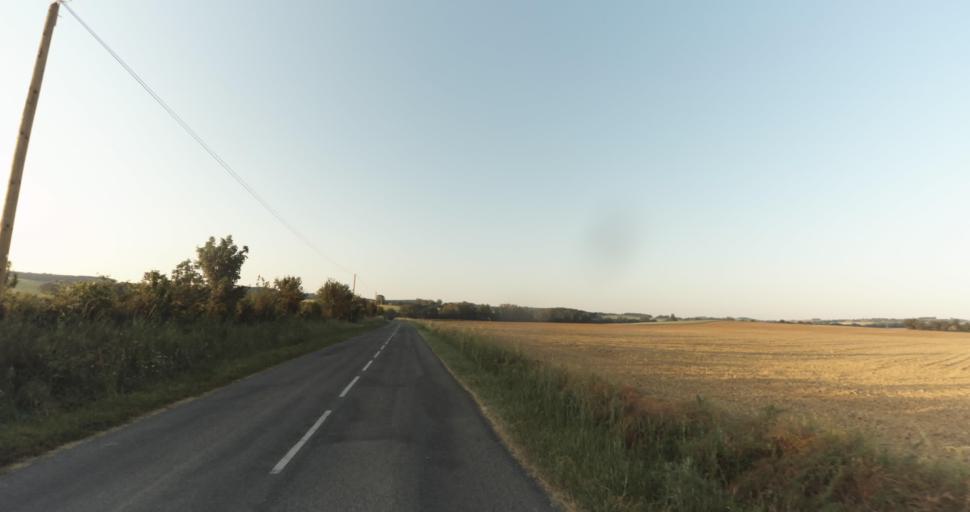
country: FR
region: Midi-Pyrenees
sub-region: Departement du Gers
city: Pujaudran
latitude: 43.6358
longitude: 1.1546
